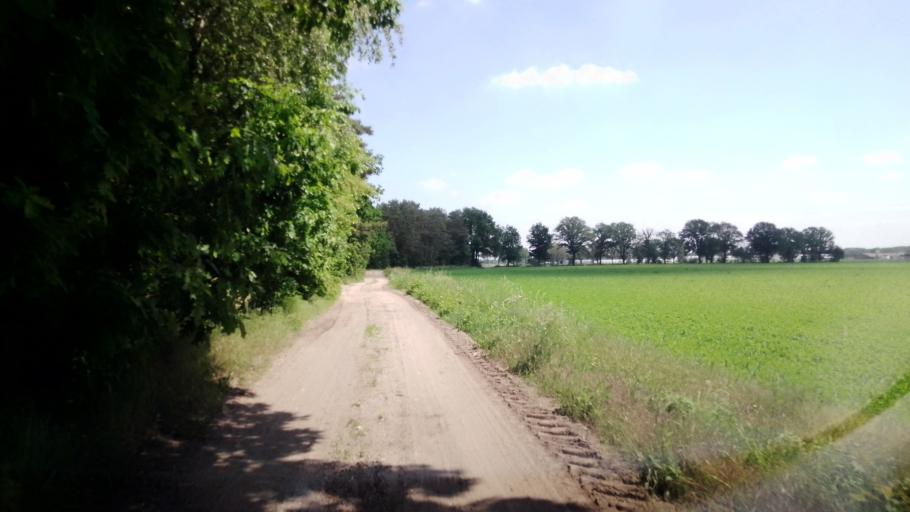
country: NL
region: Limburg
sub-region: Gemeente Beesel
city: Beesel
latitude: 51.3065
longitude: 6.0274
